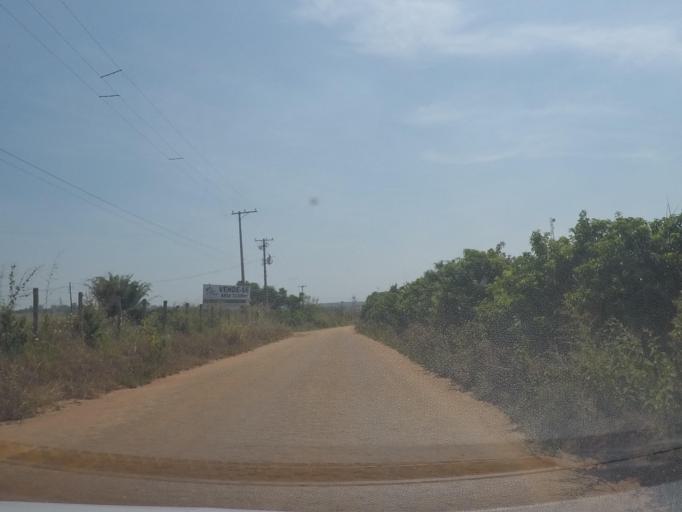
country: BR
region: Sao Paulo
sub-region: Sumare
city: Sumare
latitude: -22.8644
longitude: -47.2796
